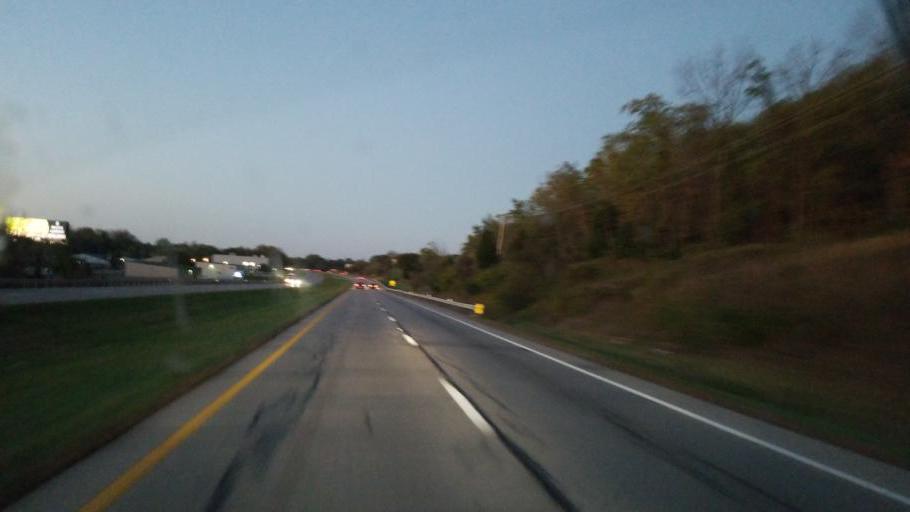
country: US
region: Ohio
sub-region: Pickaway County
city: Logan Elm Village
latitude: 39.5167
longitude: -82.9704
